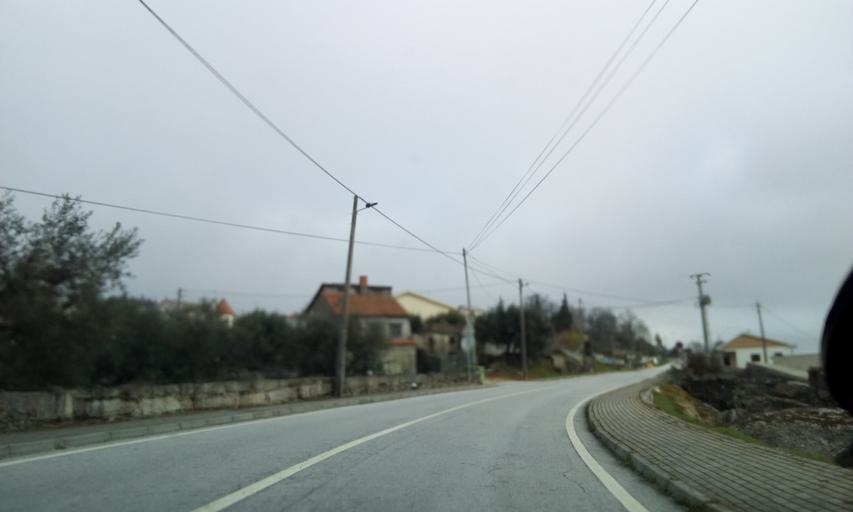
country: PT
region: Guarda
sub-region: Fornos de Algodres
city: Fornos de Algodres
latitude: 40.6832
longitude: -7.4710
